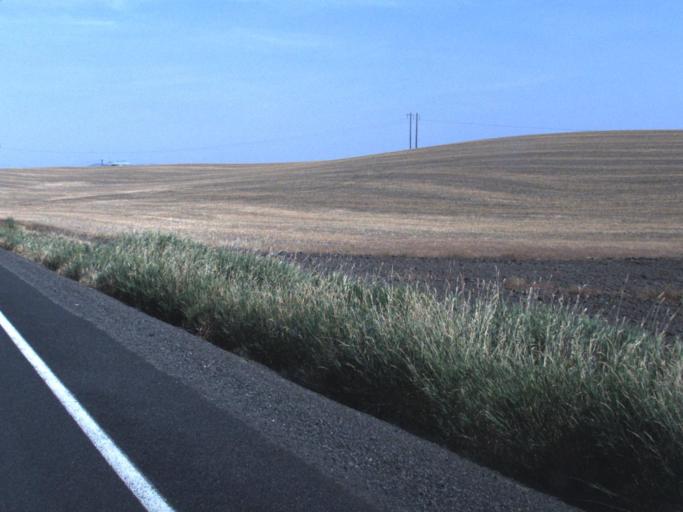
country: US
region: Idaho
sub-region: Benewah County
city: Plummer
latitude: 47.2064
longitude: -117.0891
